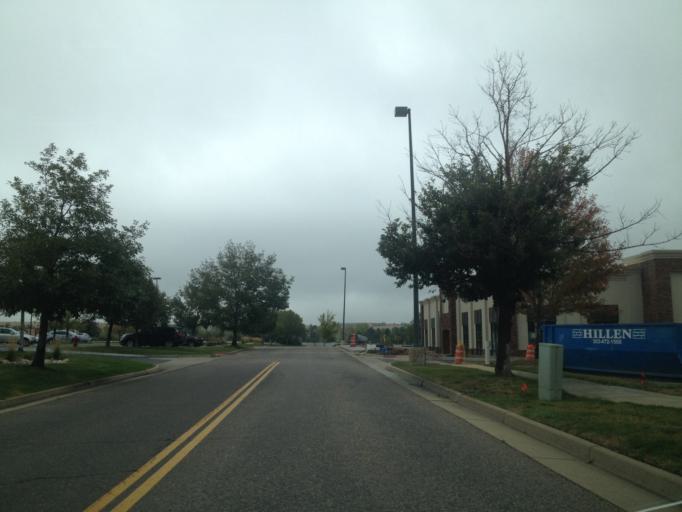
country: US
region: Colorado
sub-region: Boulder County
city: Superior
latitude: 39.9585
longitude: -105.1719
